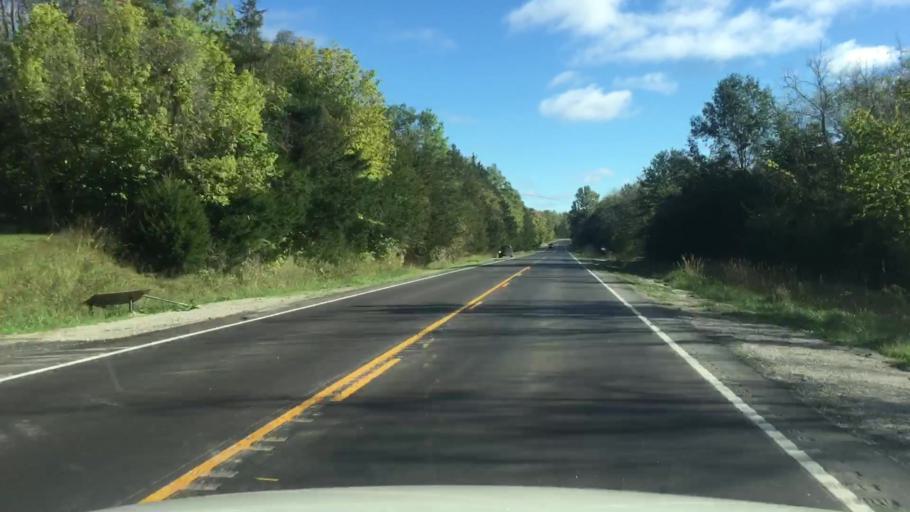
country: US
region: Missouri
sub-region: Howard County
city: New Franklin
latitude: 38.9861
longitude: -92.5390
